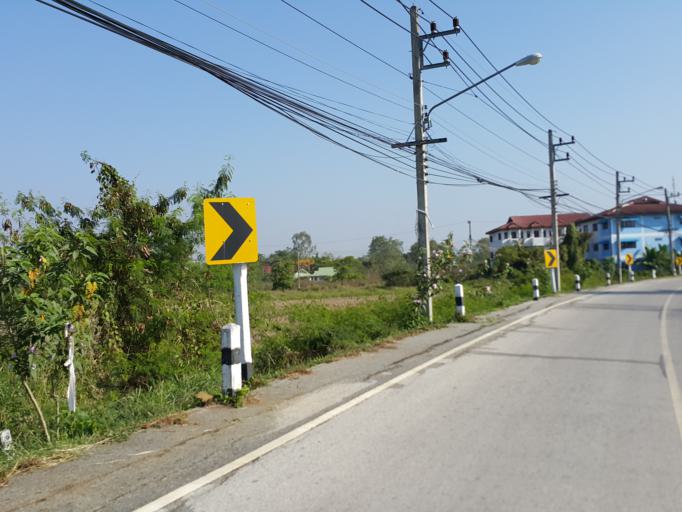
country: TH
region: Chiang Mai
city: San Kamphaeng
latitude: 18.8044
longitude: 99.1125
